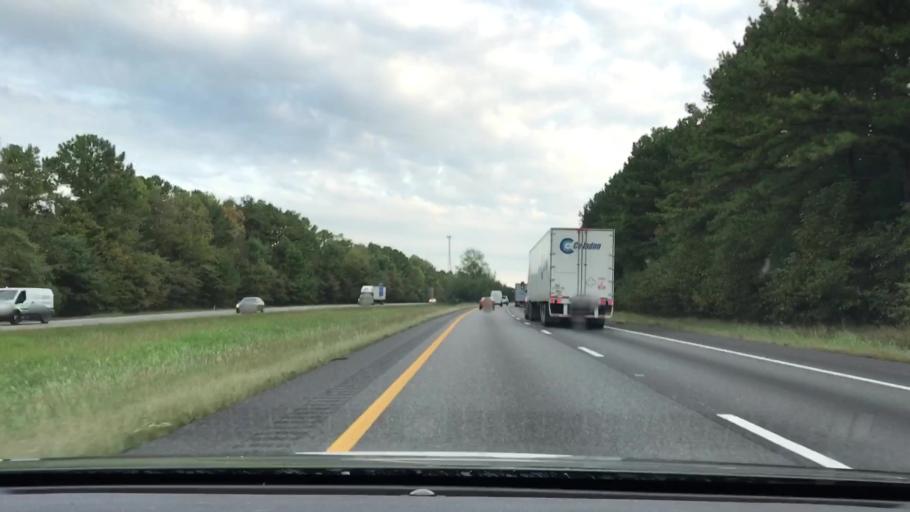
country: US
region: Tennessee
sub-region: Robertson County
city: Cross Plains
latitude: 36.5402
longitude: -86.6380
